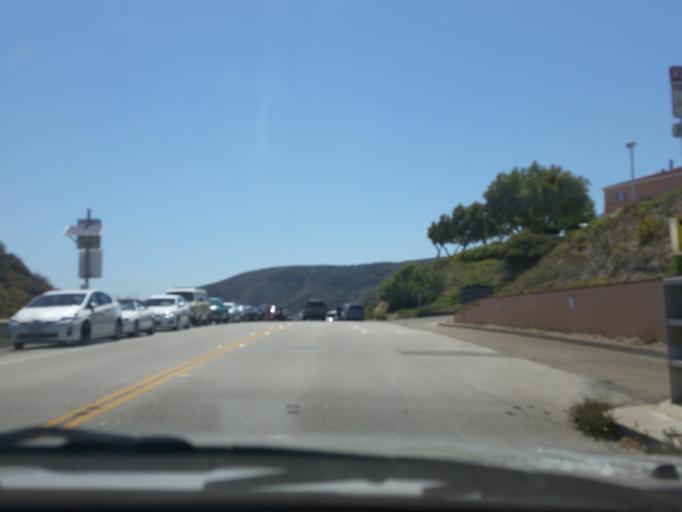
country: US
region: California
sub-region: San Luis Obispo County
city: Avila Beach
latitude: 35.1792
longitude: -120.7384
